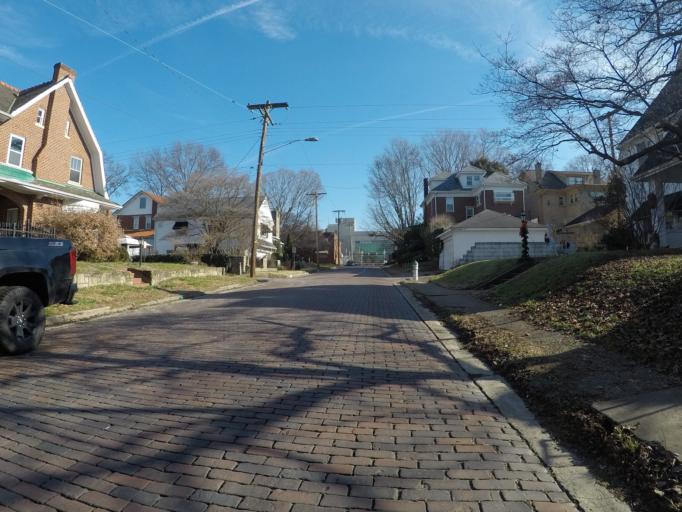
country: US
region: West Virginia
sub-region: Cabell County
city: Huntington
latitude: 38.4088
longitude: -82.4301
